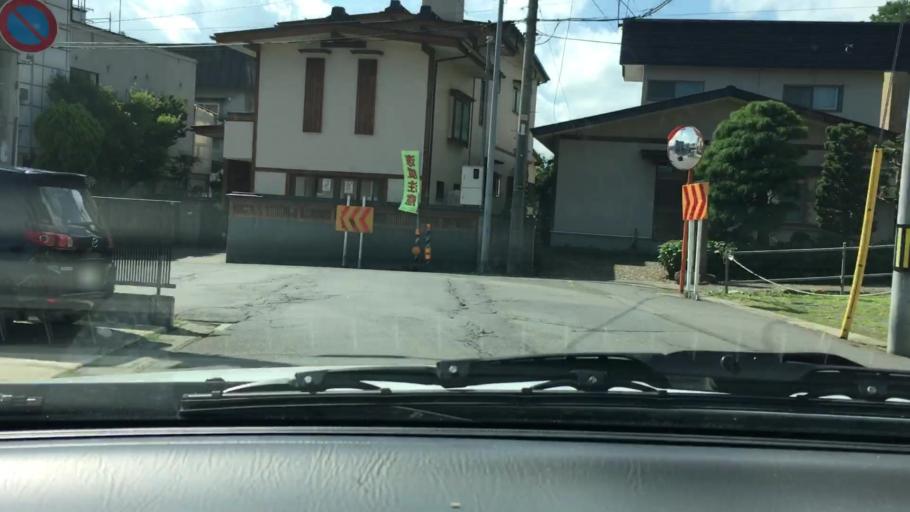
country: JP
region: Aomori
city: Hirosaki
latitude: 40.5964
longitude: 140.4697
